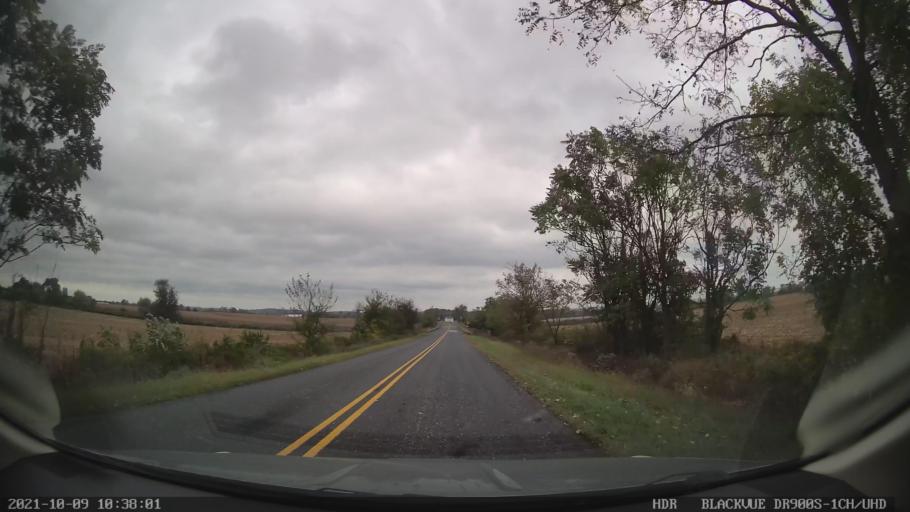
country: US
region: Pennsylvania
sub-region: Lehigh County
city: Alburtis
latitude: 40.5044
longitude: -75.6273
